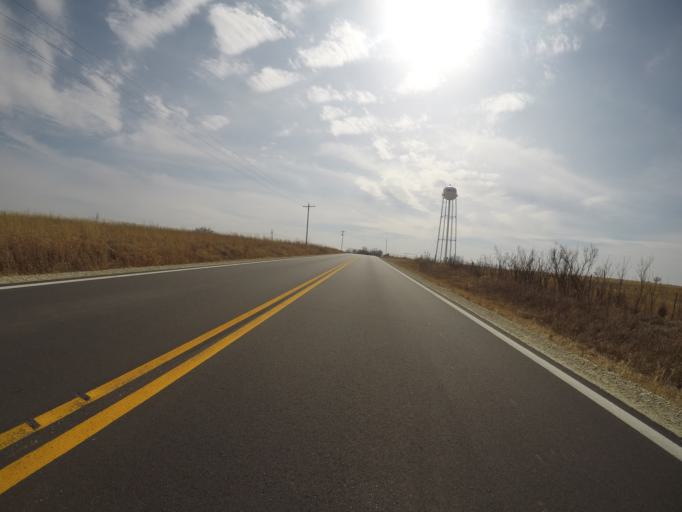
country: US
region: Kansas
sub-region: Geary County
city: Grandview Plaza
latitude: 39.0205
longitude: -96.7616
